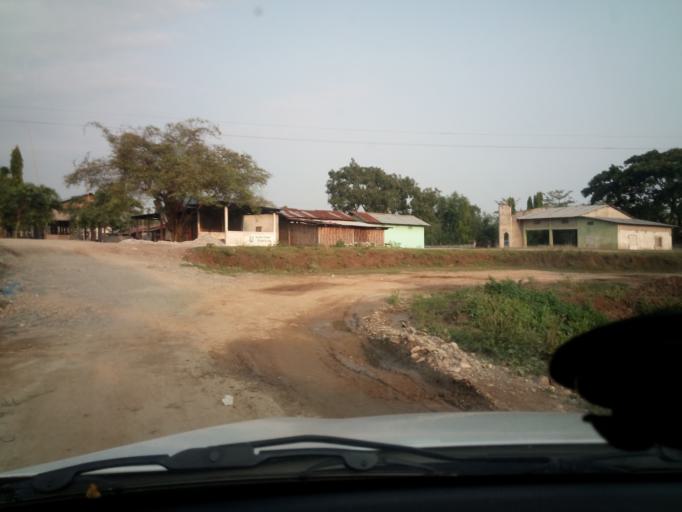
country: IN
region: Assam
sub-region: Udalguri
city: Udalguri
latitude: 26.6770
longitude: 92.0911
